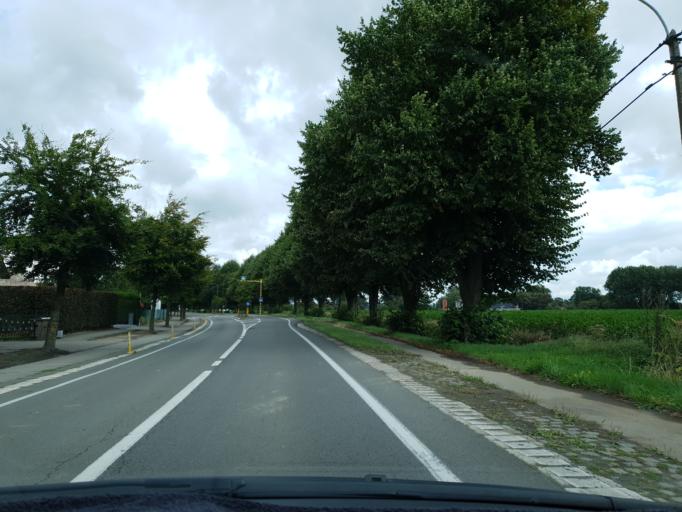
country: BE
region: Wallonia
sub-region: Province du Hainaut
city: Pecq
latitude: 50.7196
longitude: 3.3601
